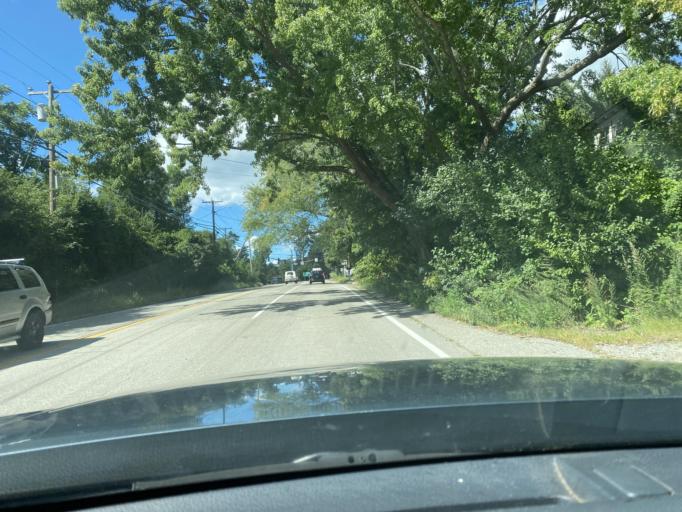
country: US
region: New Hampshire
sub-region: Rockingham County
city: Portsmouth
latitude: 43.0568
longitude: -70.7817
